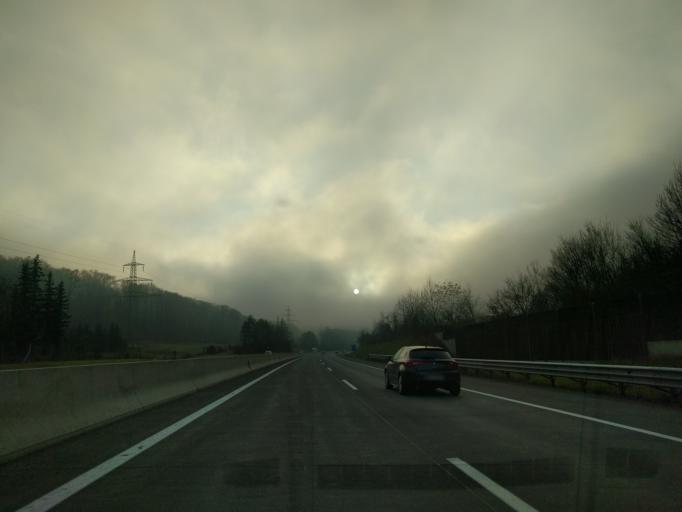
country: AT
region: Lower Austria
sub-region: Politischer Bezirk Wien-Umgebung
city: Purkersdorf
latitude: 48.1848
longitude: 16.1860
